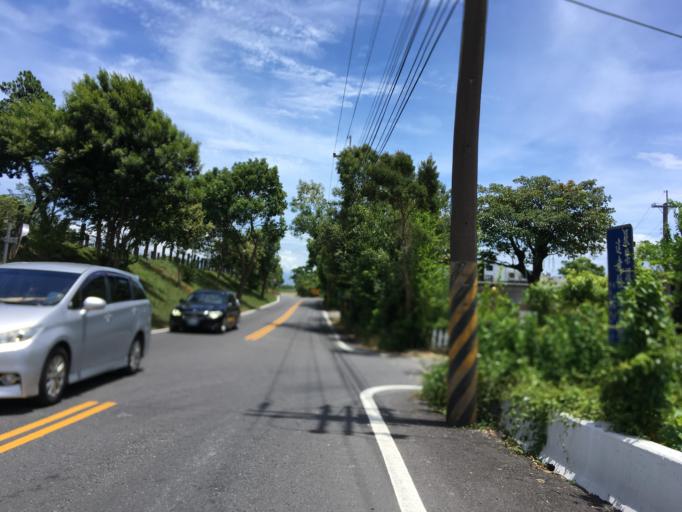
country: TW
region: Taiwan
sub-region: Yilan
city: Yilan
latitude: 24.6521
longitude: 121.7269
